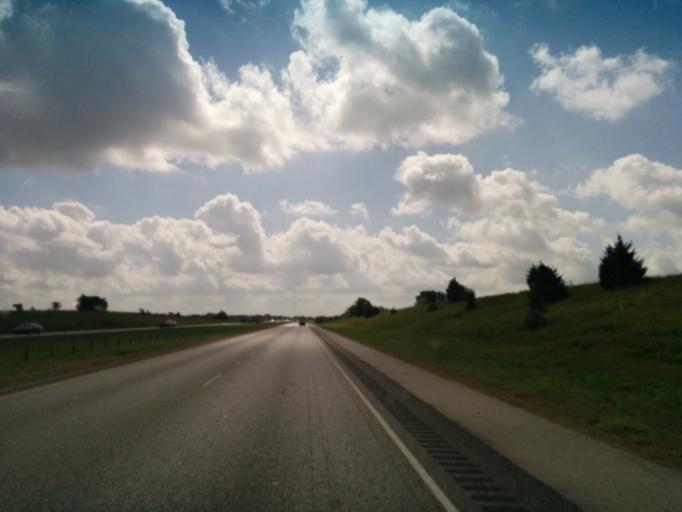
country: US
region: Texas
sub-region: Fayette County
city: Schulenburg
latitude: 29.6911
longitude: -96.9873
